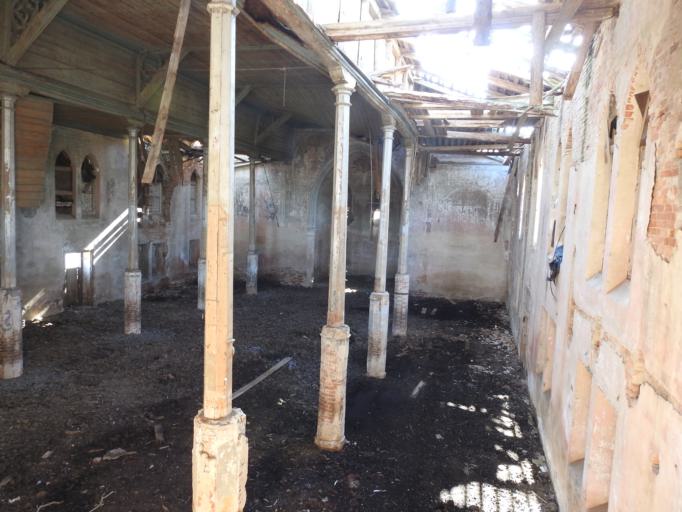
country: RU
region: Volgograd
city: Staraya Poltavka
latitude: 50.7805
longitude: 46.4149
